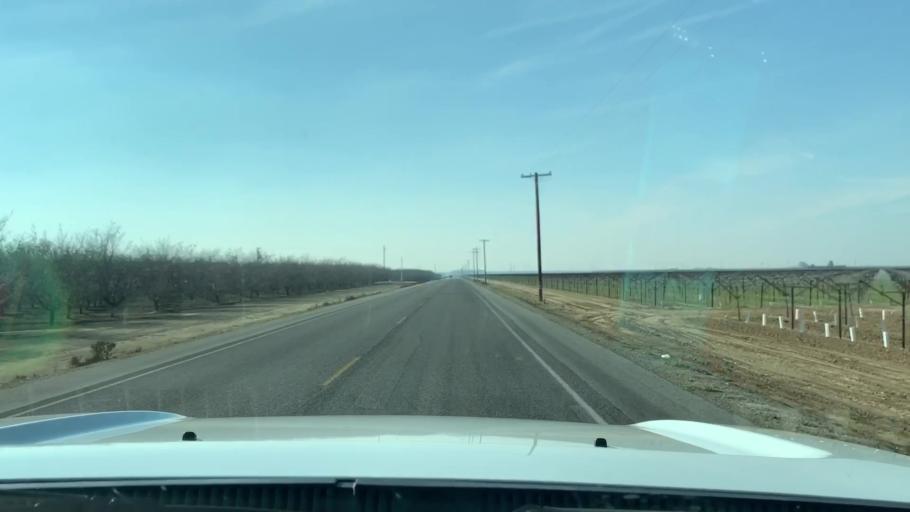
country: US
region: California
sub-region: Kern County
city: Buttonwillow
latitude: 35.5005
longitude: -119.4274
